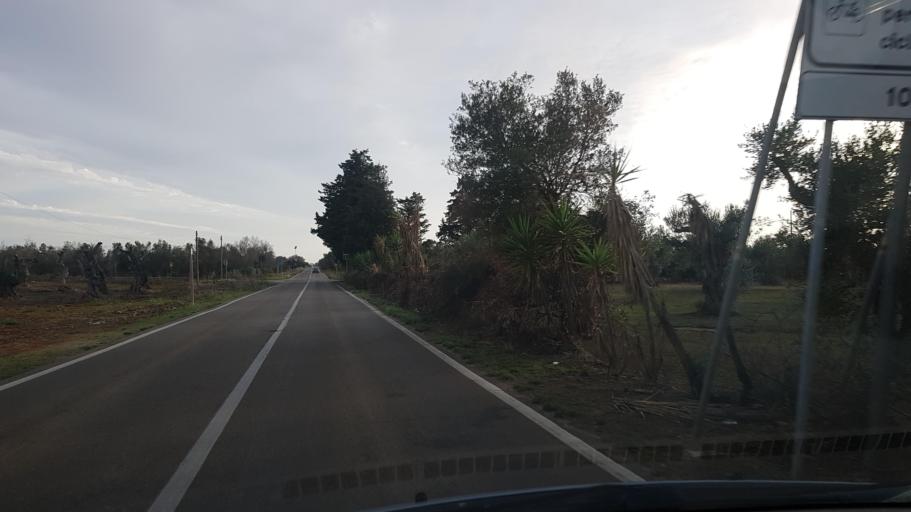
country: IT
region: Apulia
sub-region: Provincia di Brindisi
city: Torchiarolo
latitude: 40.4753
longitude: 18.1227
